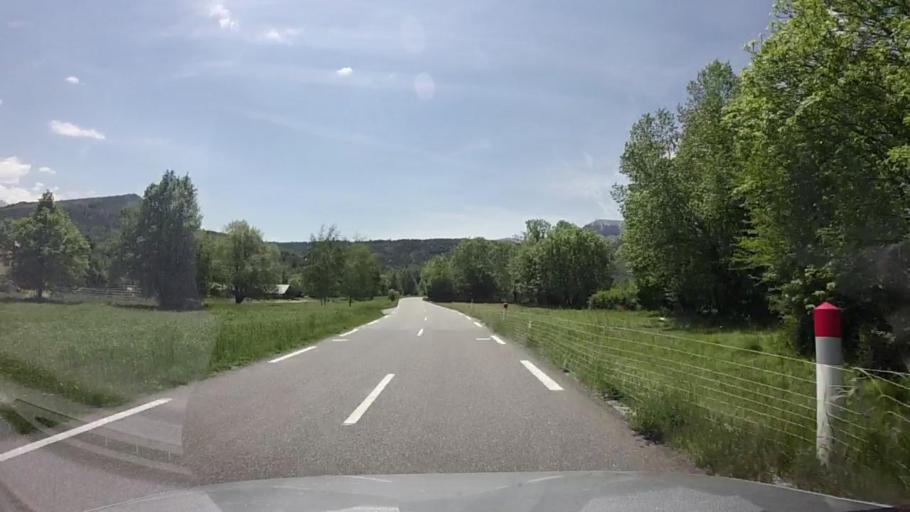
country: FR
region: Provence-Alpes-Cote d'Azur
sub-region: Departement des Alpes-de-Haute-Provence
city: Seyne-les-Alpes
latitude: 44.3835
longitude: 6.3272
